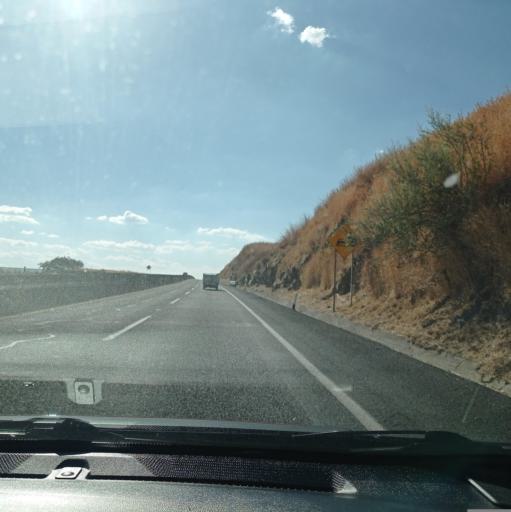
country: MX
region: Jalisco
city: Zapotlanejo
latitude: 20.6630
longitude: -103.0461
